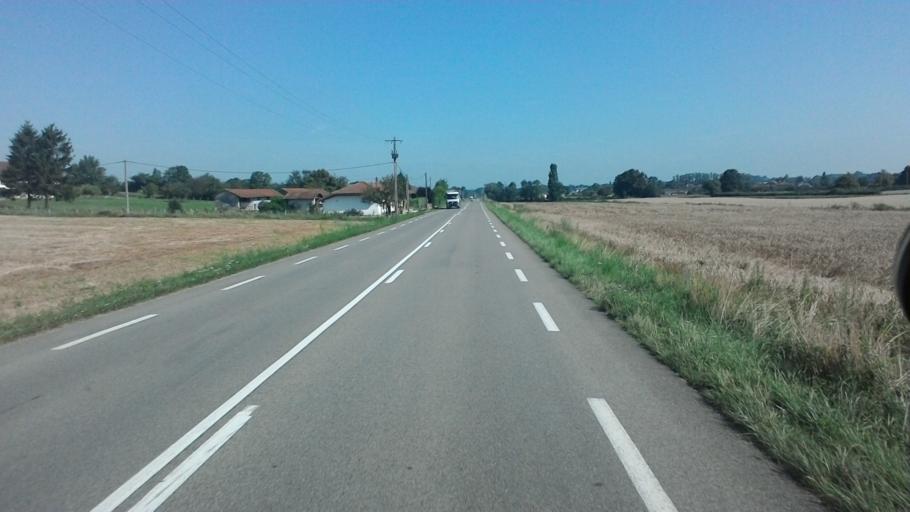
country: FR
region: Rhone-Alpes
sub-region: Departement de l'Ain
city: Montrevel-en-Bresse
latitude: 46.3827
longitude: 5.1168
